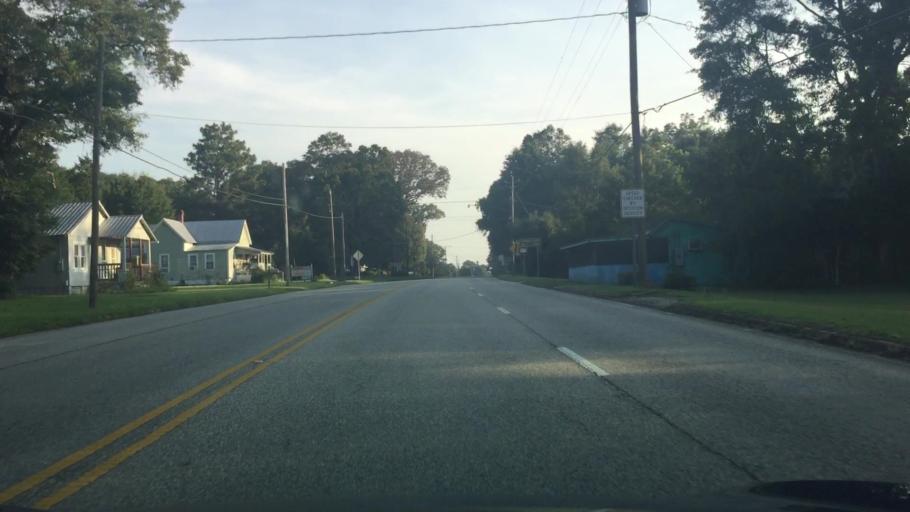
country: US
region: Alabama
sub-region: Covington County
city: Florala
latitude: 30.9955
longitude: -86.3090
